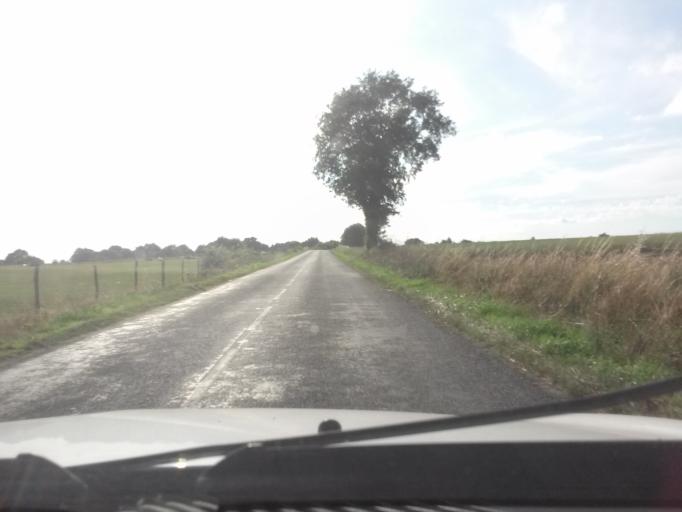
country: FR
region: Pays de la Loire
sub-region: Departement de la Vendee
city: Saint-Hilaire-de-Loulay
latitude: 46.9955
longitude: -1.3752
